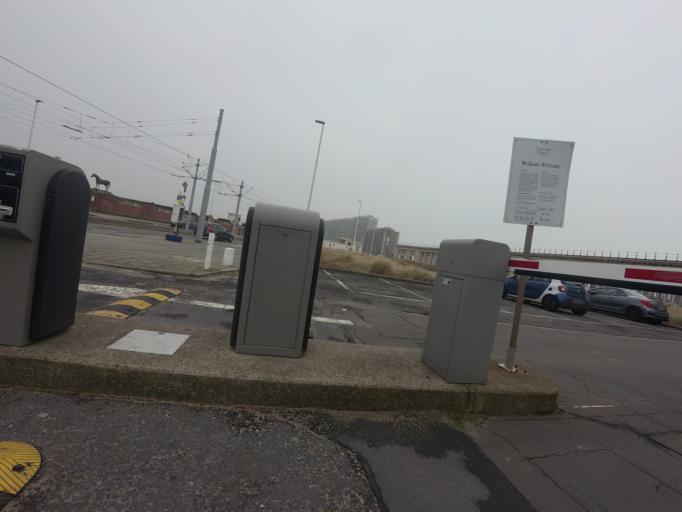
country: BE
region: Flanders
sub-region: Provincie West-Vlaanderen
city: Ostend
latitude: 51.2254
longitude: 2.9019
